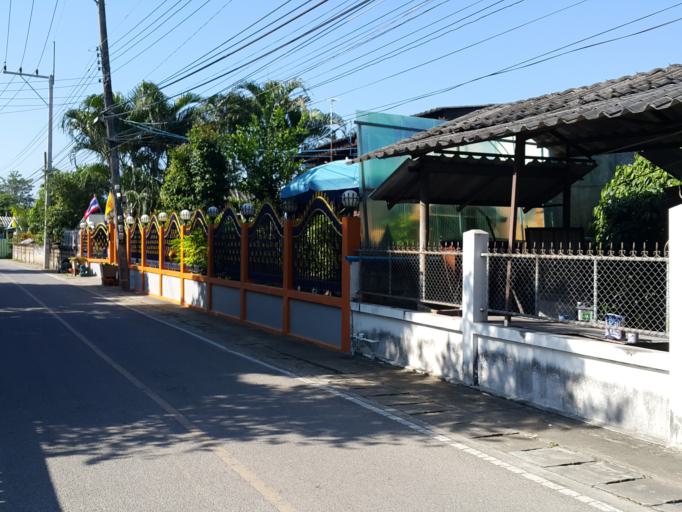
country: TH
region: Chiang Mai
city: San Kamphaeng
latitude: 18.7512
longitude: 99.0732
